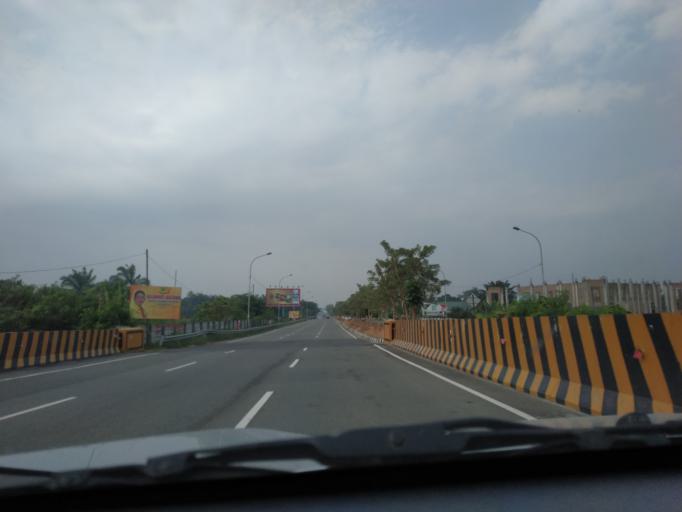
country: ID
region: North Sumatra
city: Percut
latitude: 3.6059
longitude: 98.8498
